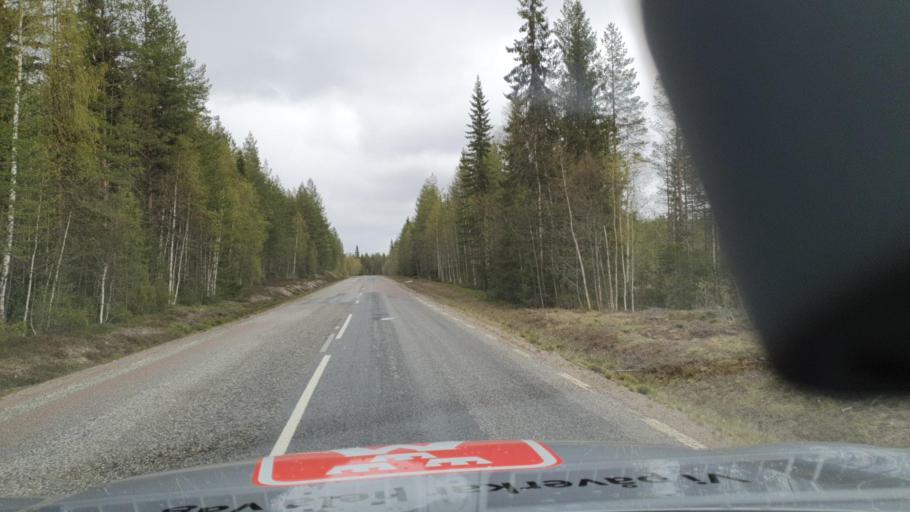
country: SE
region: Vaesternorrland
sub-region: Solleftea Kommun
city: Solleftea
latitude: 63.6554
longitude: 17.3092
